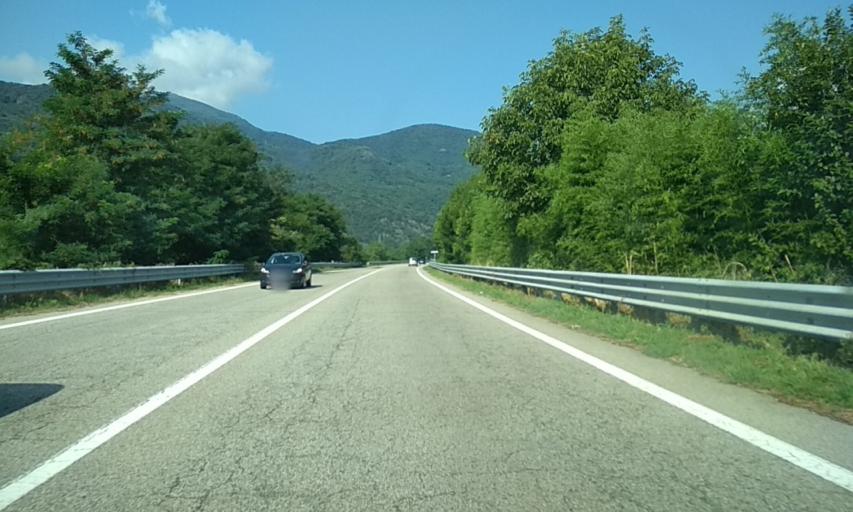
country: IT
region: Piedmont
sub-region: Provincia di Torino
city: Cuorgne
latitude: 45.4027
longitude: 7.6408
